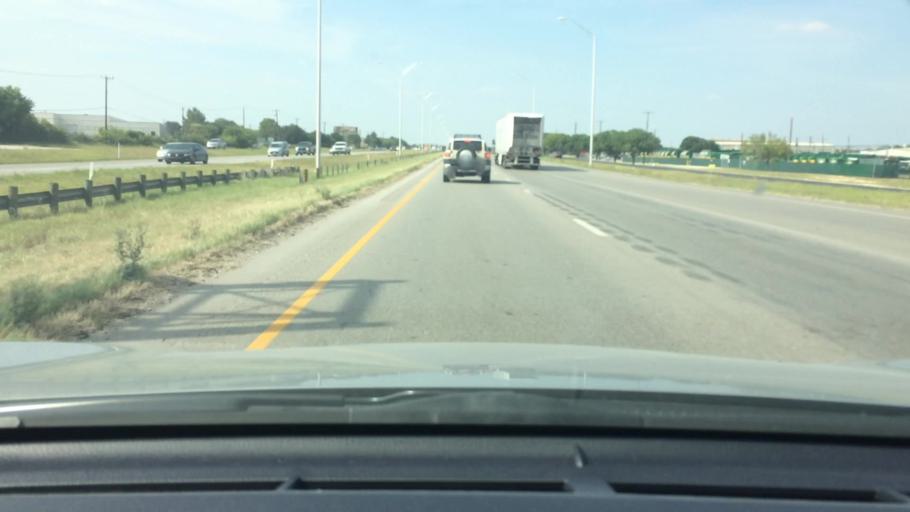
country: US
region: Texas
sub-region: Bexar County
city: China Grove
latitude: 29.3756
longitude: -98.3937
